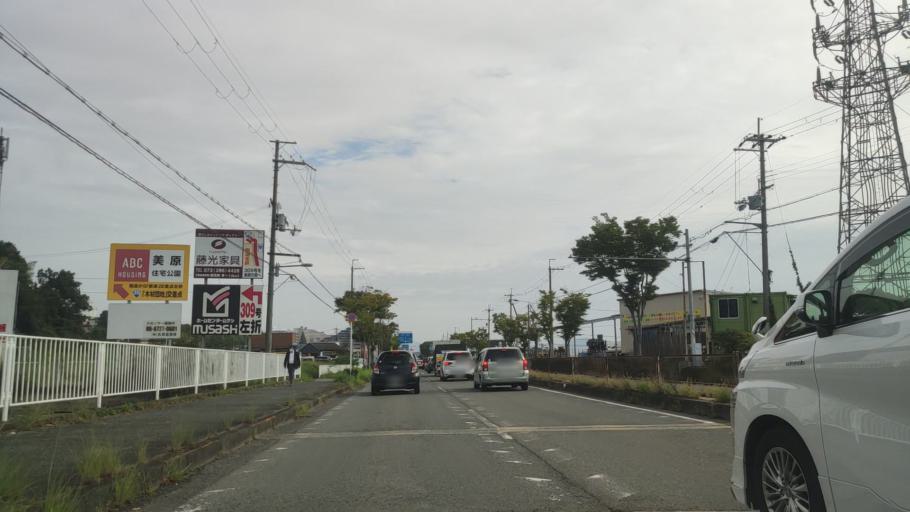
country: JP
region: Osaka
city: Tondabayashicho
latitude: 34.4856
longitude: 135.5805
